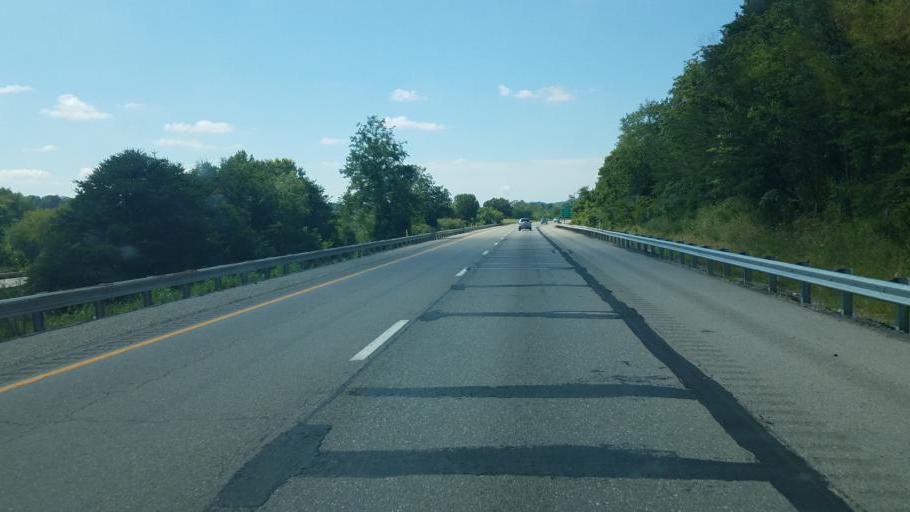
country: US
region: West Virginia
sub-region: Jackson County
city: Ripley
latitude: 38.7469
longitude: -81.6803
